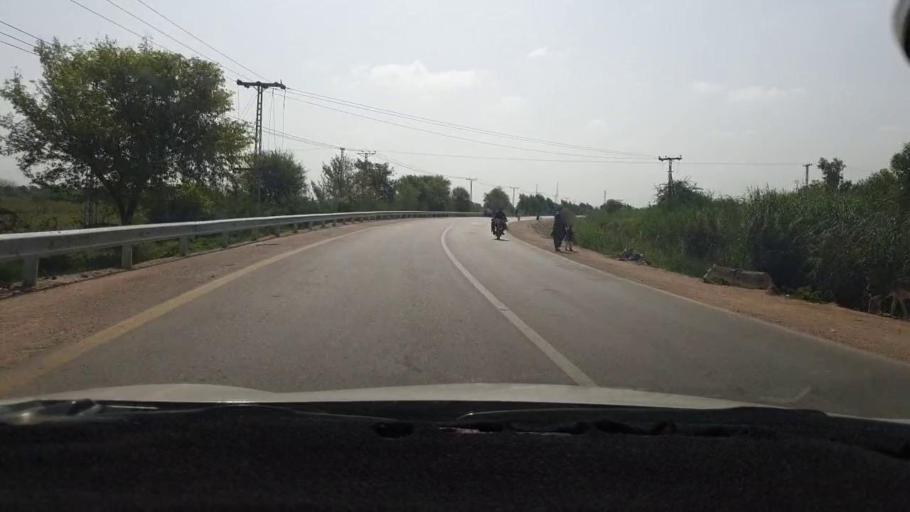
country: PK
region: Sindh
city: Mirpur Khas
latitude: 25.7196
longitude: 69.1192
